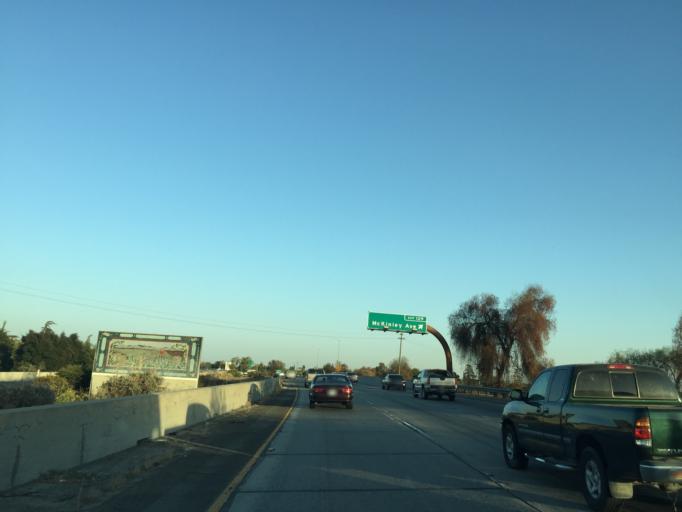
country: US
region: California
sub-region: Fresno County
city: Fresno
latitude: 36.7686
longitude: -119.7825
